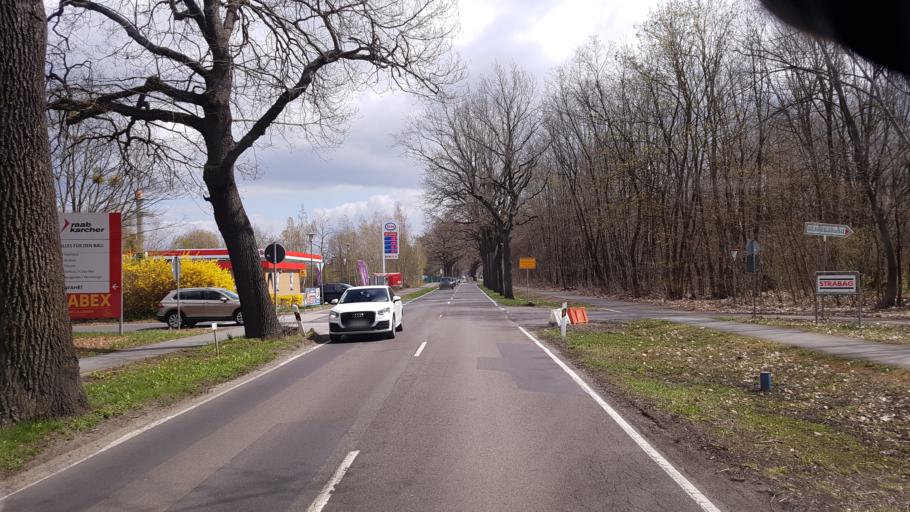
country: DE
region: Brandenburg
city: Senftenberg
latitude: 51.5257
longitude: 13.9714
